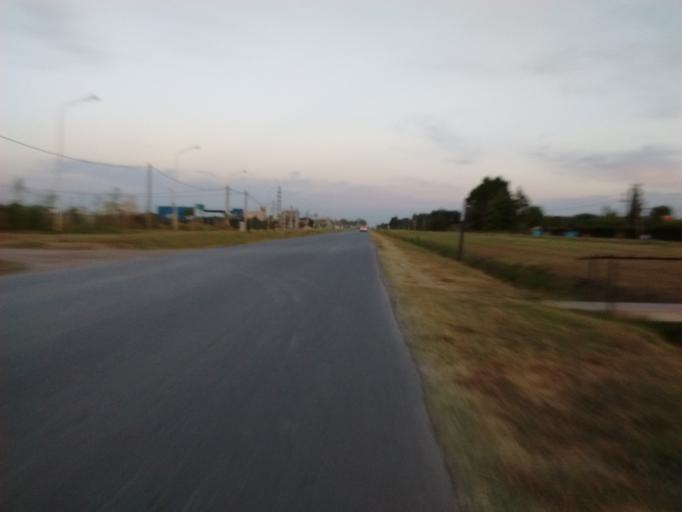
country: AR
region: Santa Fe
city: Roldan
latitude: -32.9029
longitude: -60.8886
